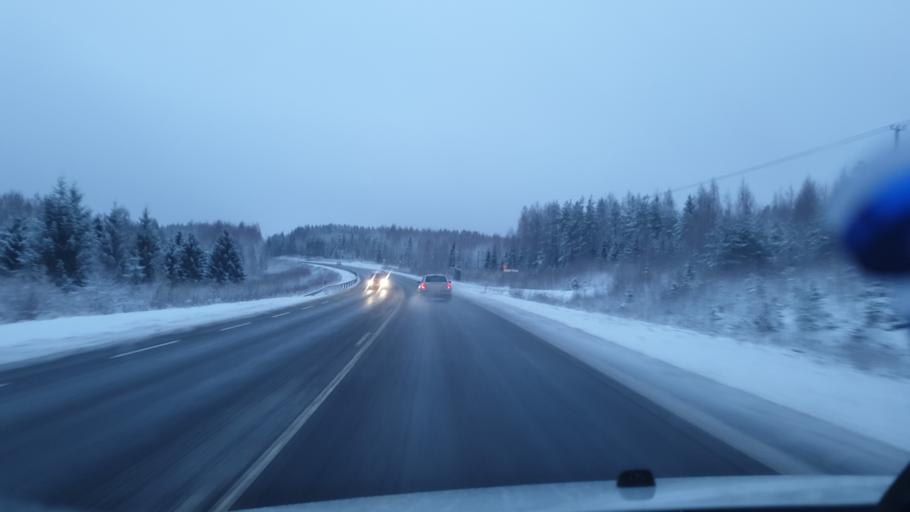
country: FI
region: Central Finland
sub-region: Saarijaervi-Viitasaari
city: Viitasaari
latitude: 63.1279
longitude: 25.7739
